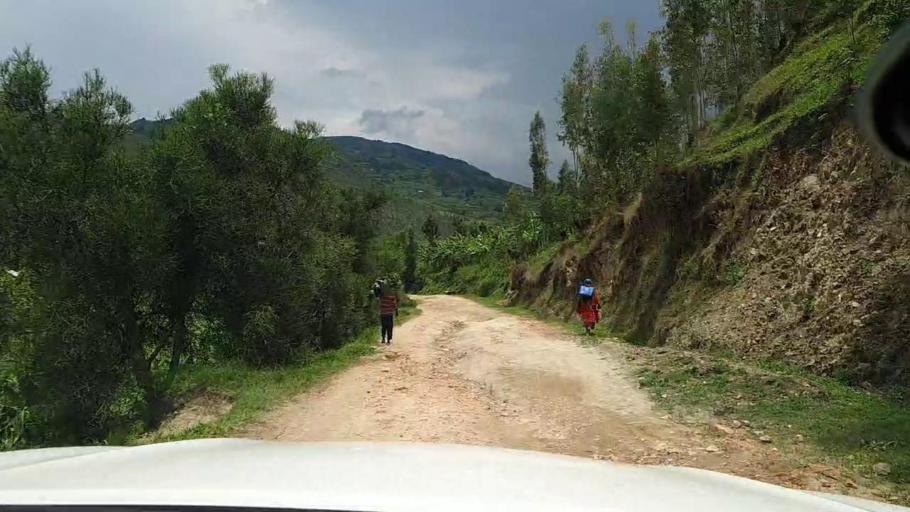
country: RW
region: Western Province
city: Kibuye
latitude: -2.0721
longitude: 29.4327
